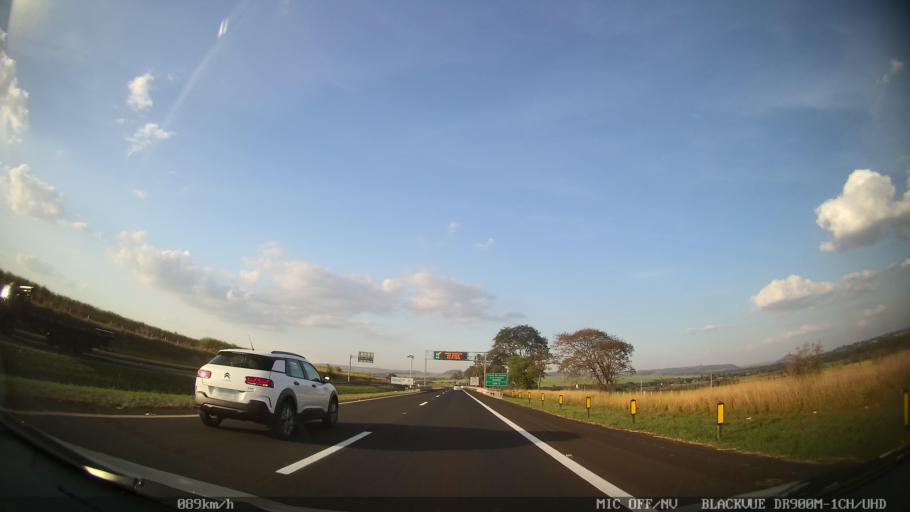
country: BR
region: Sao Paulo
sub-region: Ribeirao Preto
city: Ribeirao Preto
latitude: -21.1094
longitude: -47.7729
